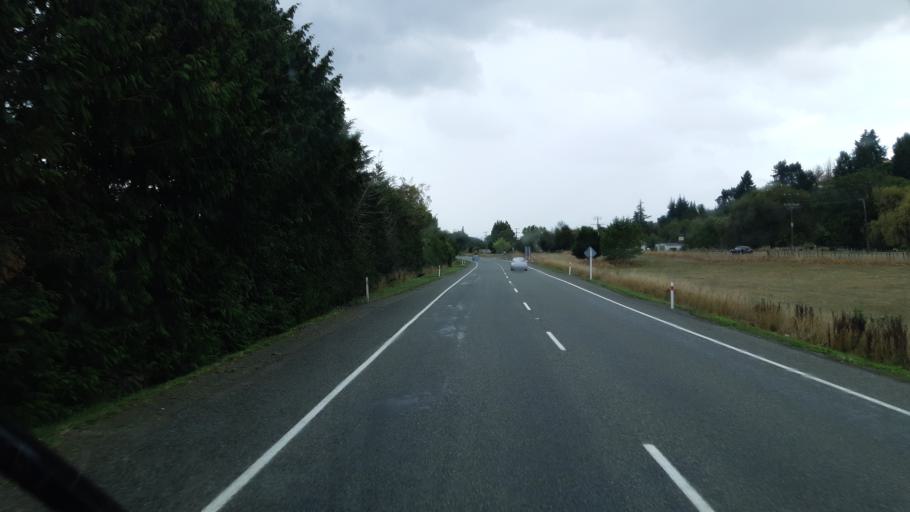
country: NZ
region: Tasman
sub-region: Tasman District
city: Wakefield
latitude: -41.4107
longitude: 173.0219
